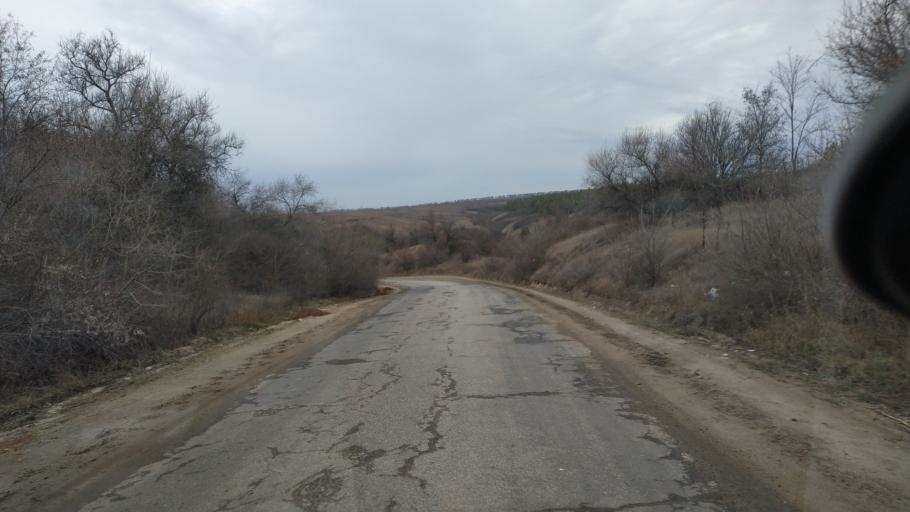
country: MD
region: Telenesti
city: Cocieri
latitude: 47.2688
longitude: 29.0797
